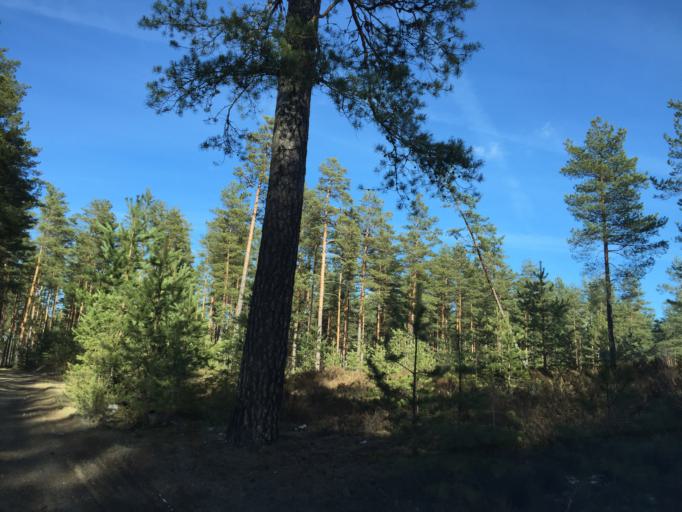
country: LV
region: Garkalne
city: Garkalne
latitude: 56.9633
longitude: 24.4571
